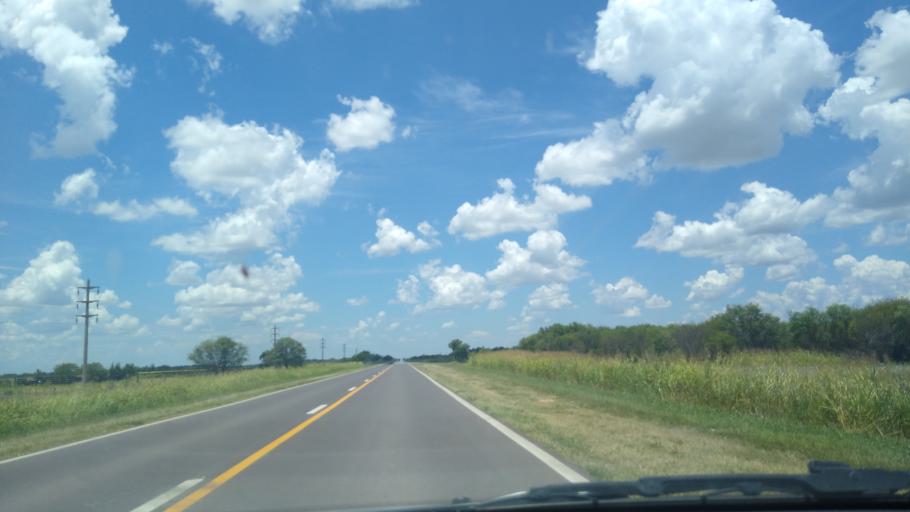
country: AR
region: Chaco
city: Presidencia Roque Saenz Pena
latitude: -26.7348
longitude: -60.3843
